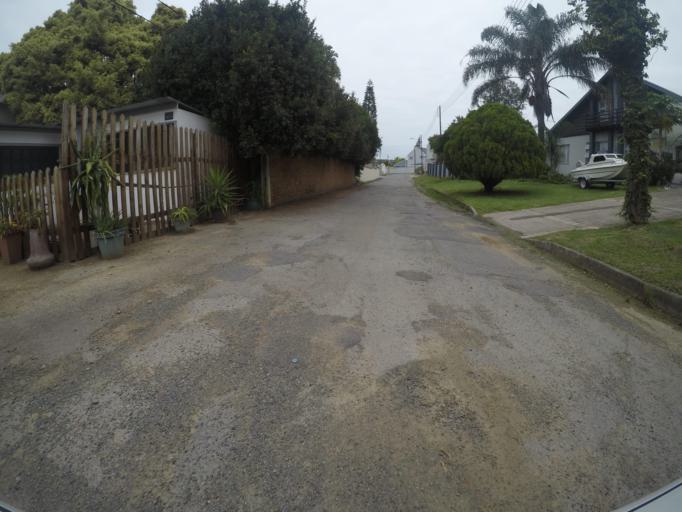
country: ZA
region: Eastern Cape
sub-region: Buffalo City Metropolitan Municipality
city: East London
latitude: -32.9723
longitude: 27.9294
